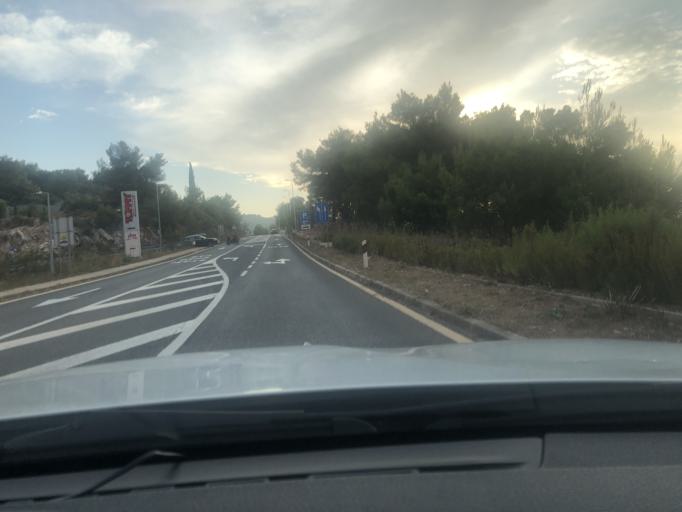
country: HR
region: Splitsko-Dalmatinska
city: Stari Grad
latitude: 43.1801
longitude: 16.5761
